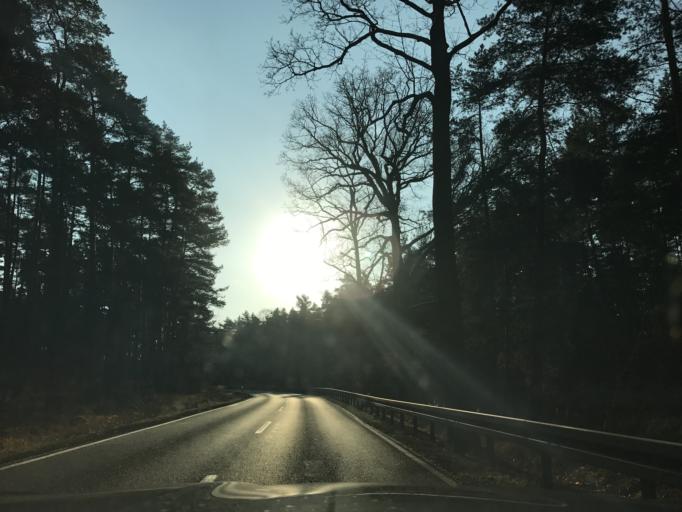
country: DE
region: Brandenburg
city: Wenzlow
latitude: 52.3560
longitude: 12.5002
